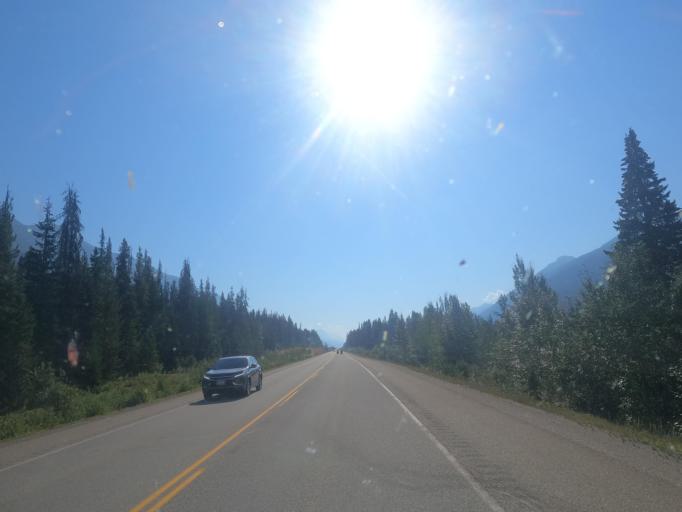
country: CA
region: Alberta
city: Grande Cache
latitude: 52.9908
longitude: -119.0113
